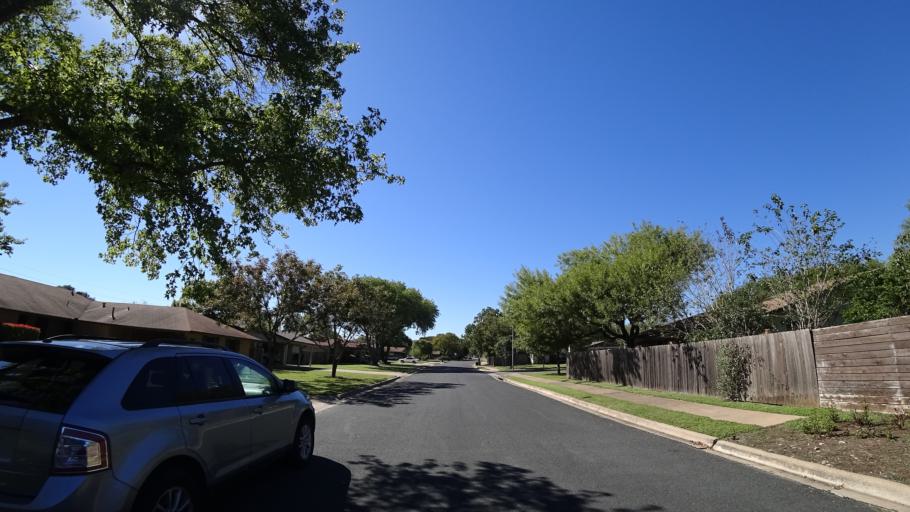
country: US
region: Texas
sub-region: Travis County
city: Rollingwood
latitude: 30.2180
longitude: -97.7993
